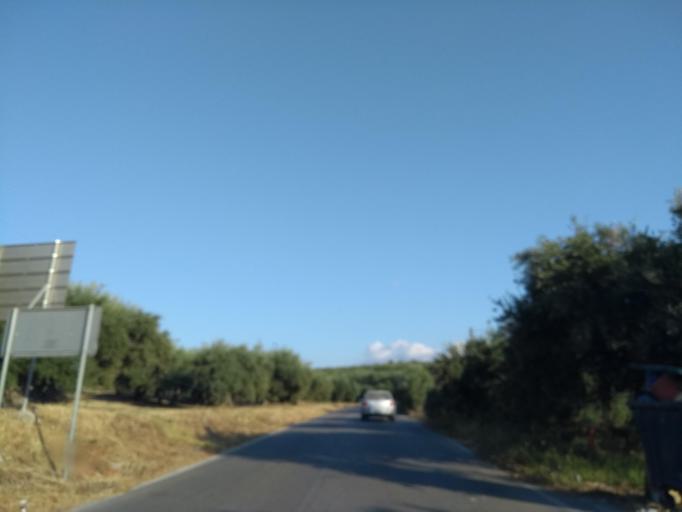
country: GR
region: Crete
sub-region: Nomos Chanias
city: Kalivai
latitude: 35.4480
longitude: 24.1753
